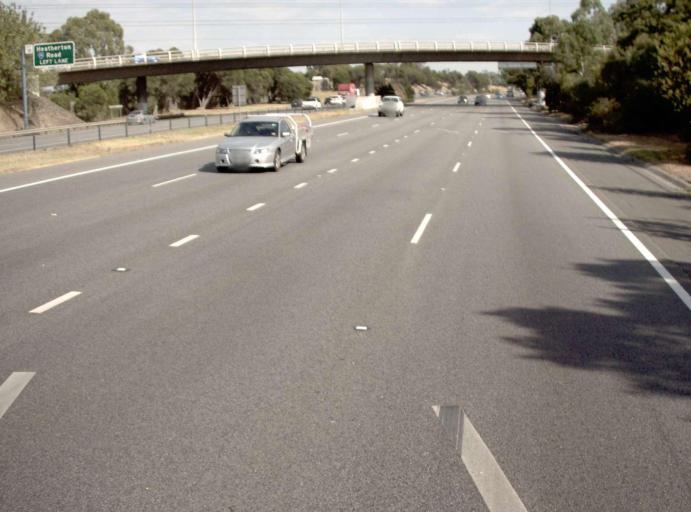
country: AU
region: Victoria
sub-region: Casey
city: Doveton
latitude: -37.9791
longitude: 145.2422
